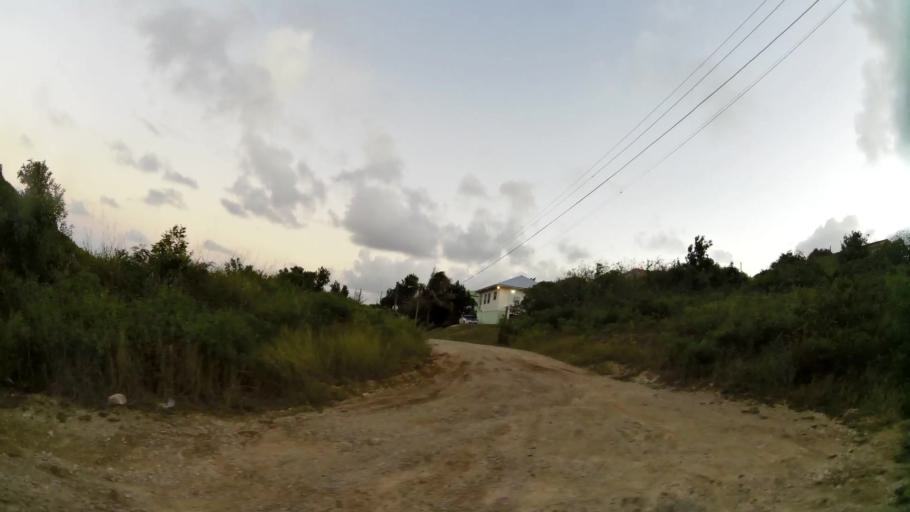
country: AG
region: Saint George
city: Piggotts
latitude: 17.1362
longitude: -61.8048
